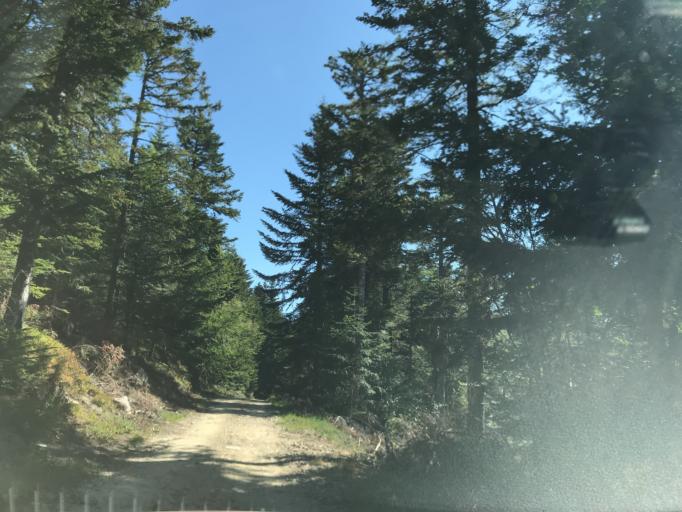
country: FR
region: Rhone-Alpes
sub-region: Departement de la Loire
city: Noiretable
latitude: 45.7636
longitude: 3.7638
